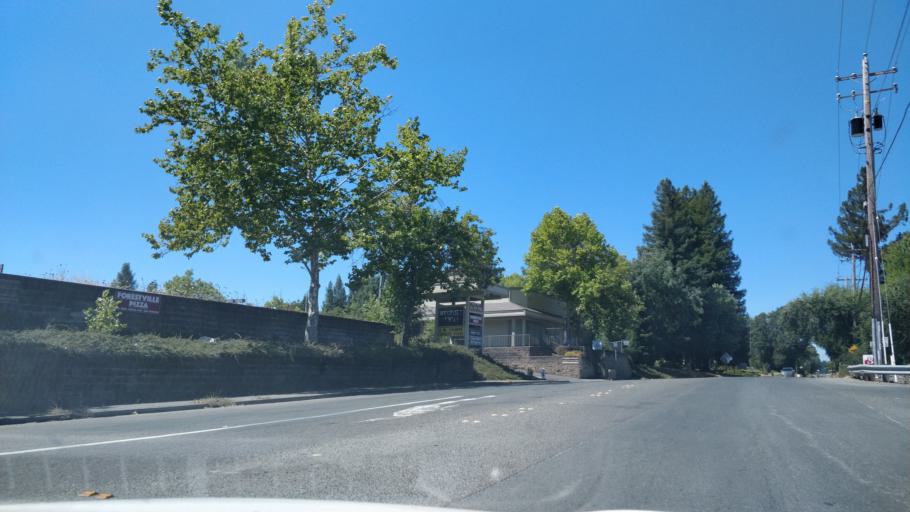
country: US
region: California
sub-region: Sonoma County
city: Forestville
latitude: 38.4738
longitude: -122.8948
